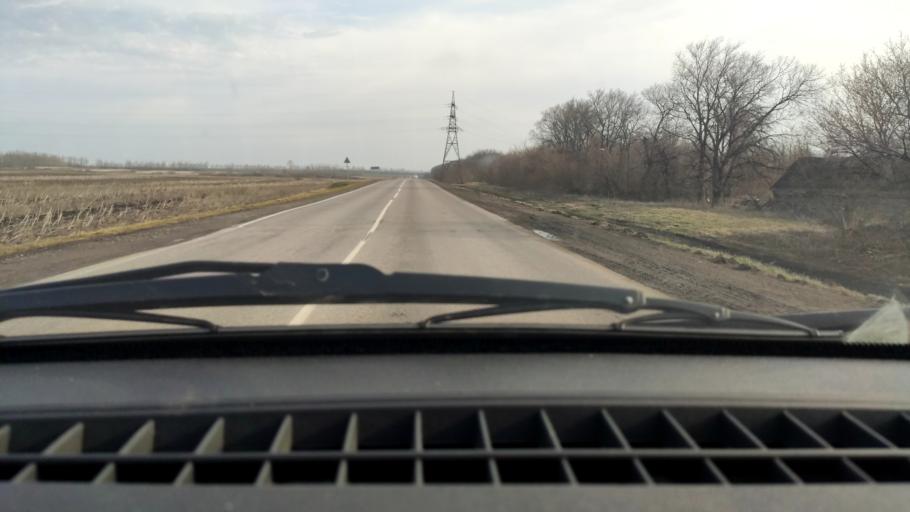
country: RU
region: Bashkortostan
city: Chishmy
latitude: 54.4796
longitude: 55.2681
